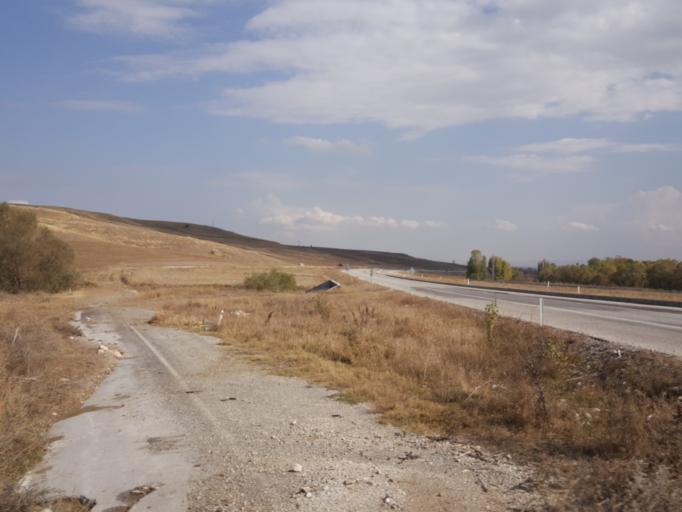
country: TR
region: Corum
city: Alaca
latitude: 40.1559
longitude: 34.6878
